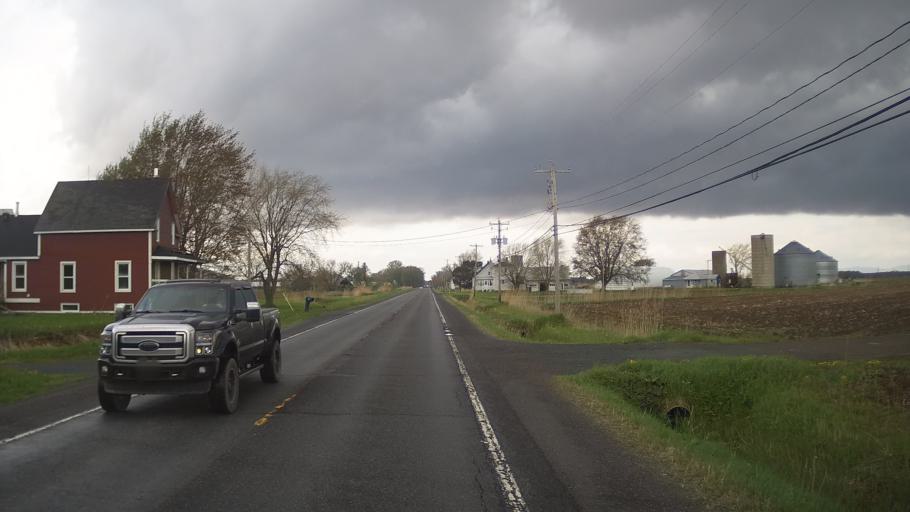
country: CA
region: Quebec
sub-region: Monteregie
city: Rougemont
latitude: 45.3342
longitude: -73.0808
